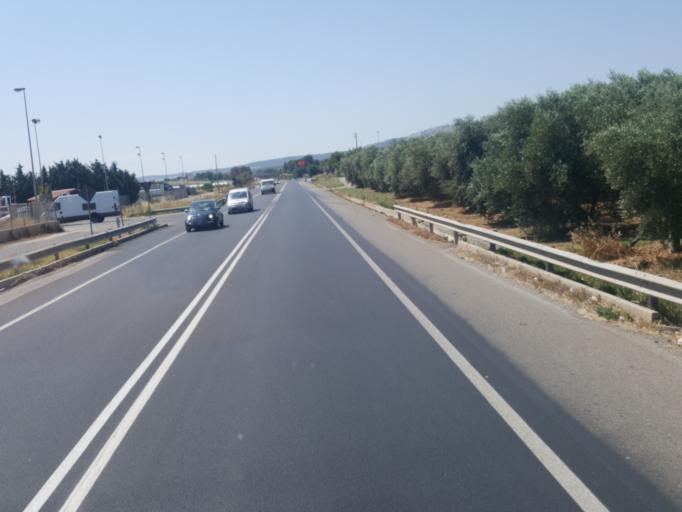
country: IT
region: Apulia
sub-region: Provincia di Taranto
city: Massafra
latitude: 40.5935
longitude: 17.0918
